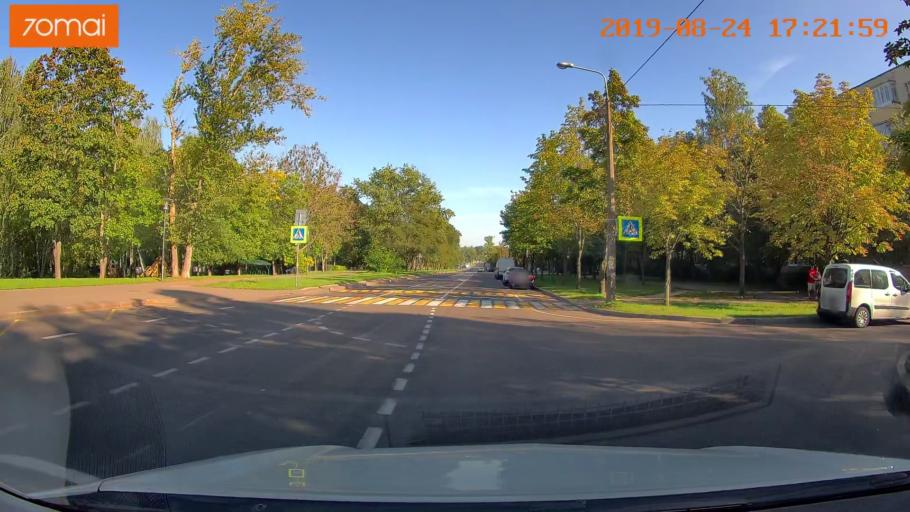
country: BY
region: Minsk
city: Hatava
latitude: 53.8477
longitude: 27.6402
